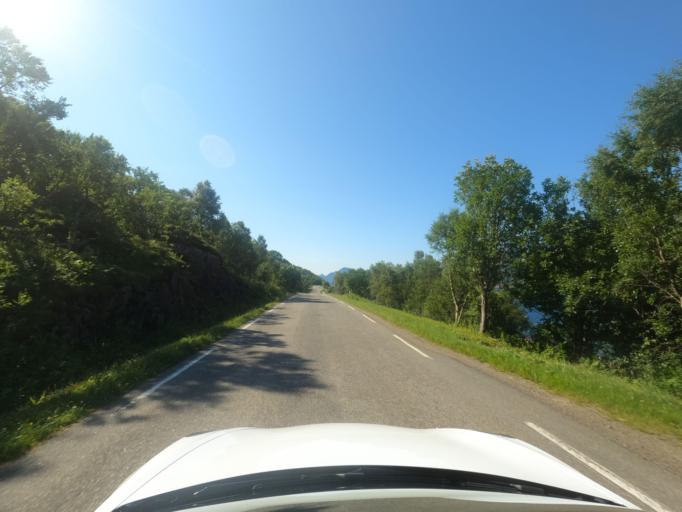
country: NO
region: Nordland
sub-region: Hadsel
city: Stokmarknes
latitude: 68.3802
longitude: 15.0871
